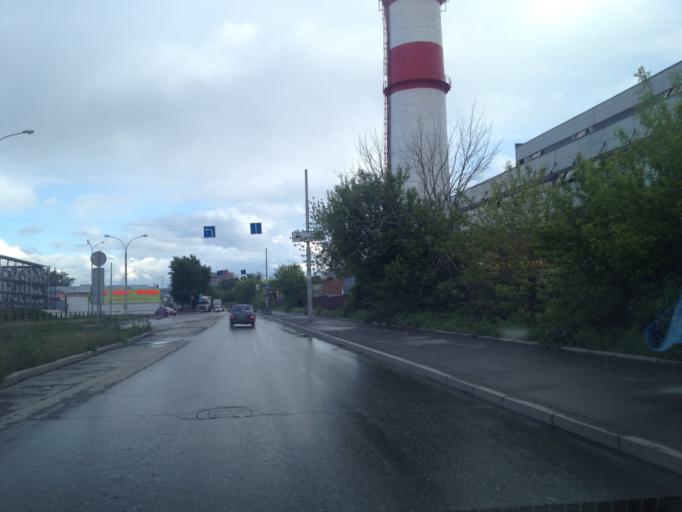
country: RU
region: Sverdlovsk
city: Yekaterinburg
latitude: 56.8510
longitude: 60.5495
